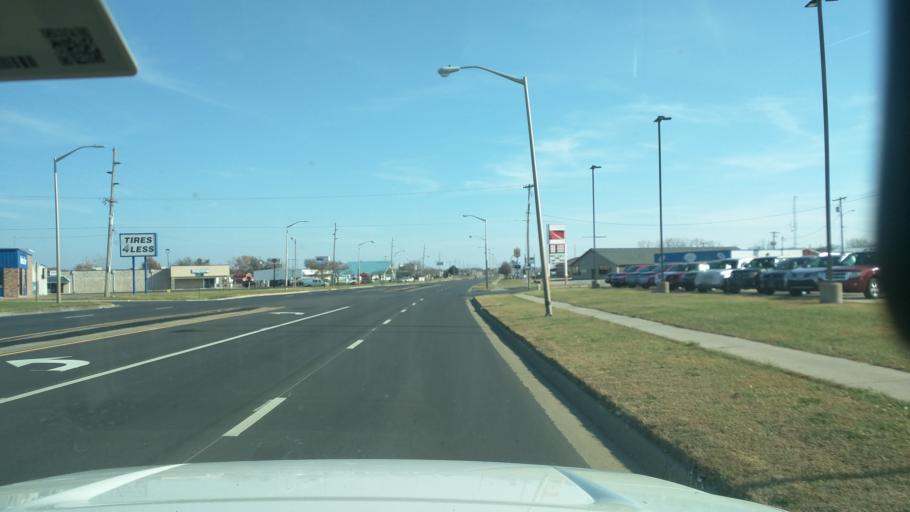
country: US
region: Kansas
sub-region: Lyon County
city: Emporia
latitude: 38.4107
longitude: -96.2225
